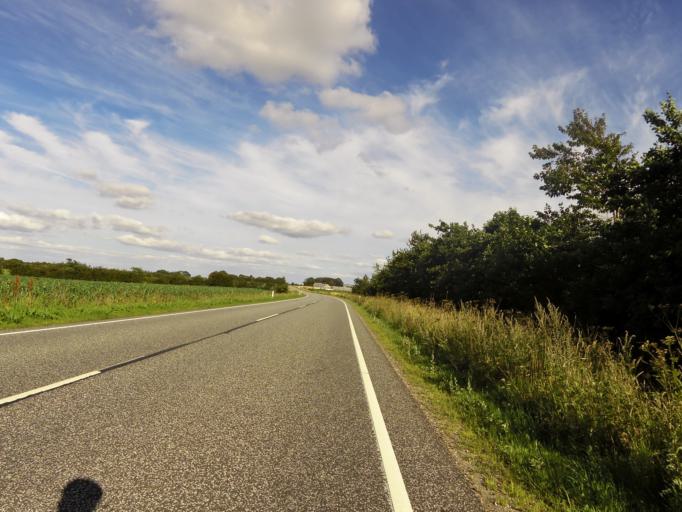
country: DK
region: South Denmark
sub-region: Haderslev Kommune
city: Gram
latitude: 55.2304
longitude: 8.9721
